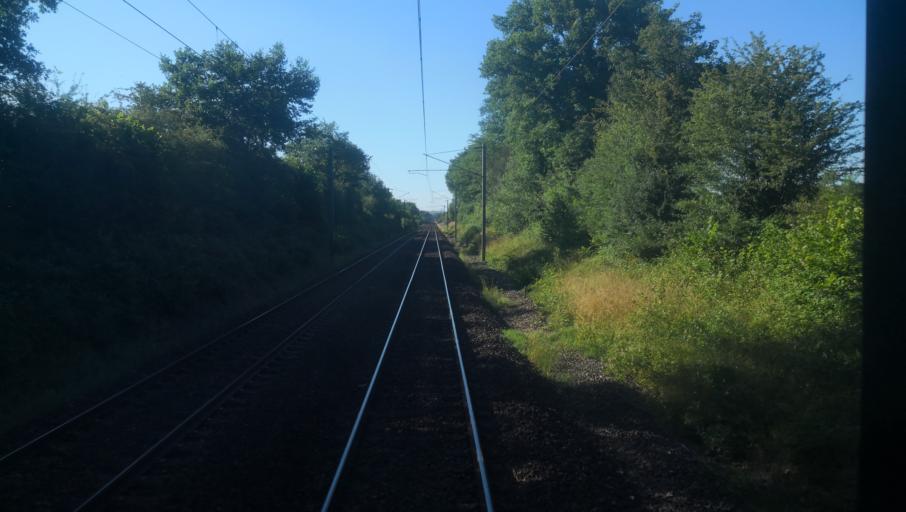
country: FR
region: Bourgogne
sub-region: Departement de la Nievre
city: La Charite-sur-Loire
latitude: 47.2290
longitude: 3.0139
